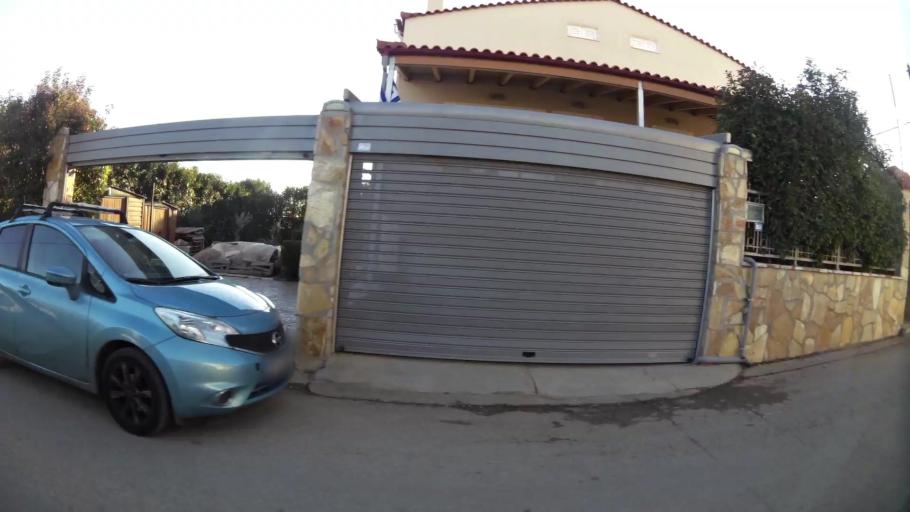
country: GR
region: Attica
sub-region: Nomarchia Anatolikis Attikis
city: Anoixi
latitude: 38.1355
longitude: 23.8551
